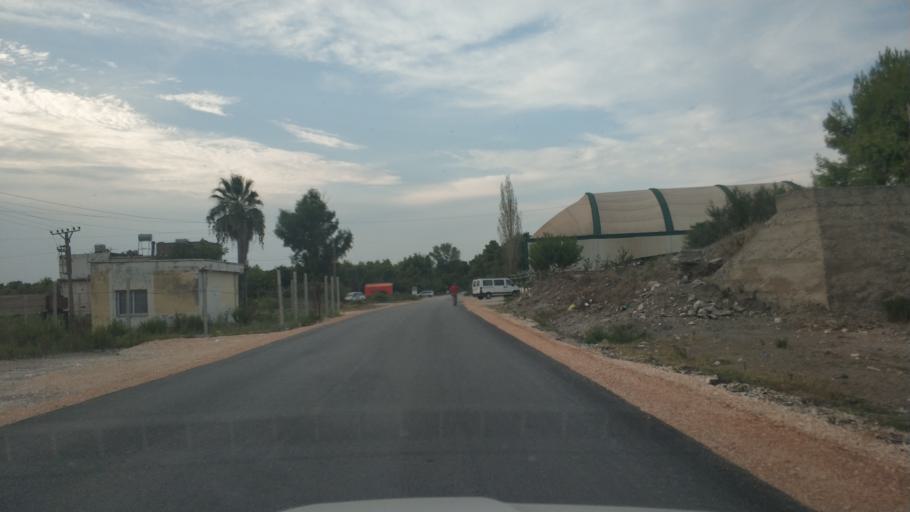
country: AL
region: Vlore
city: Vlore
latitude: 40.4765
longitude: 19.4533
